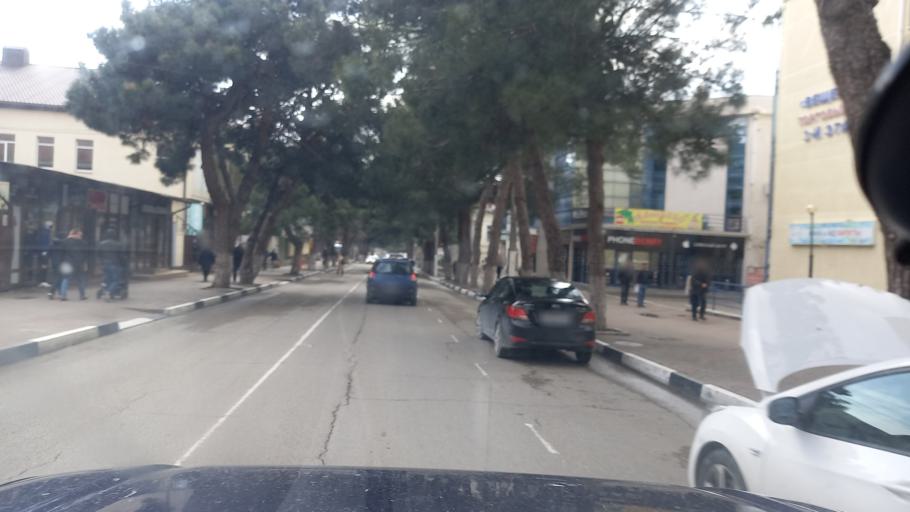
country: RU
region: Krasnodarskiy
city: Gelendzhik
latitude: 44.5635
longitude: 38.0818
